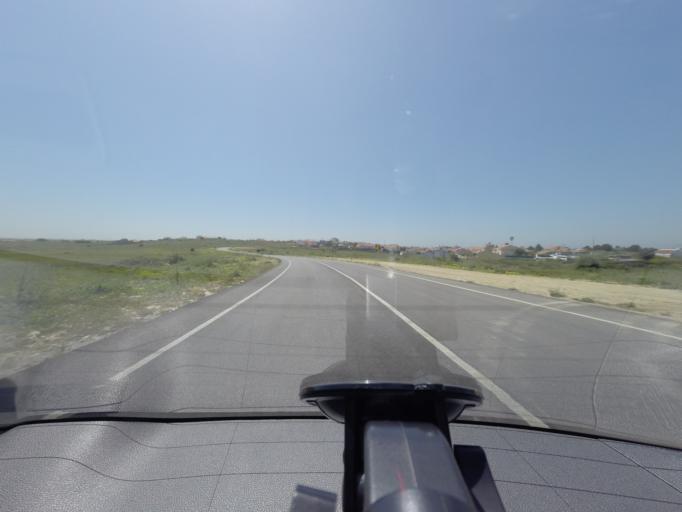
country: PT
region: Lisbon
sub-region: Cascais
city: Parede
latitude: 38.7206
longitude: -9.3587
